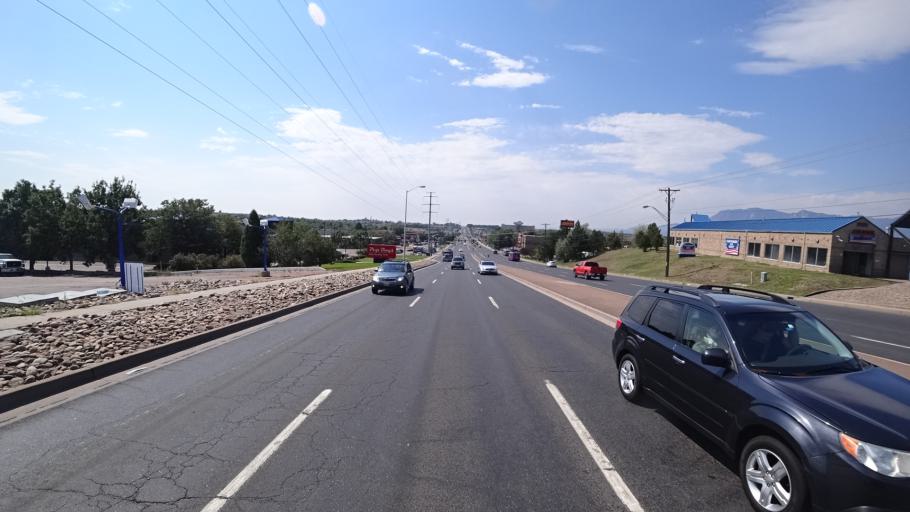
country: US
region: Colorado
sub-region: El Paso County
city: Cimarron Hills
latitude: 38.8338
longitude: -104.7574
